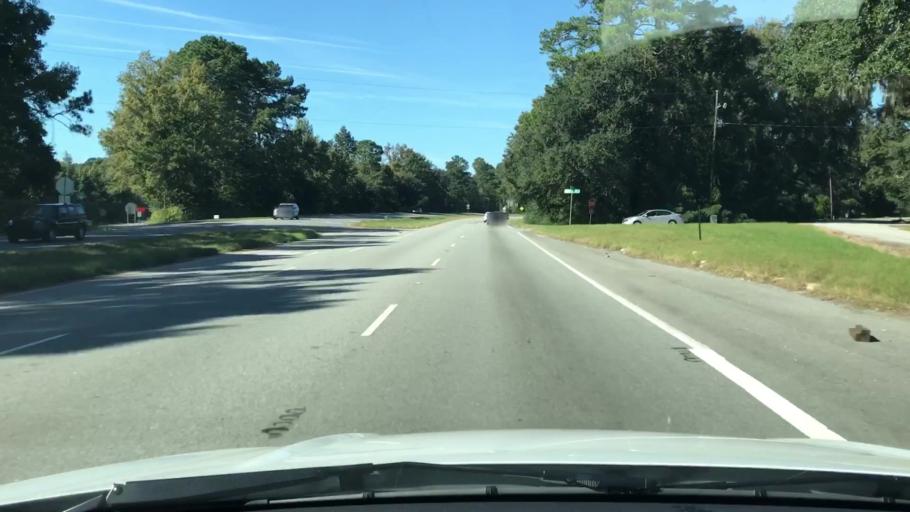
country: US
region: South Carolina
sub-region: Beaufort County
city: Laurel Bay
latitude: 32.5116
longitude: -80.7500
